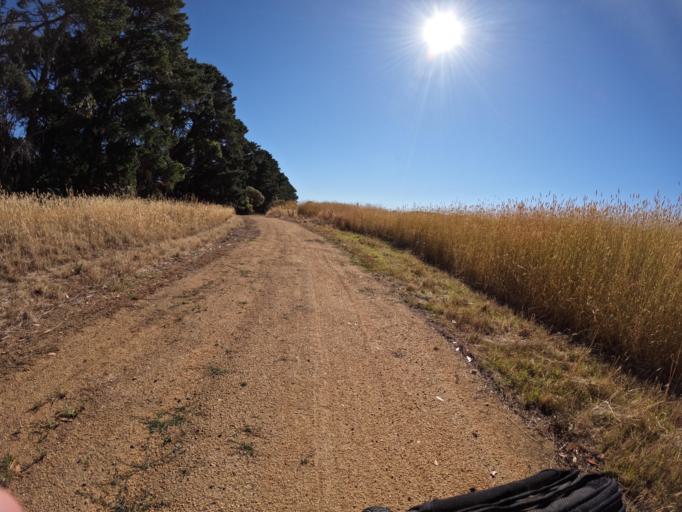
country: AU
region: Victoria
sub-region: Ballarat North
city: Delacombe
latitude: -37.6939
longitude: 143.3703
